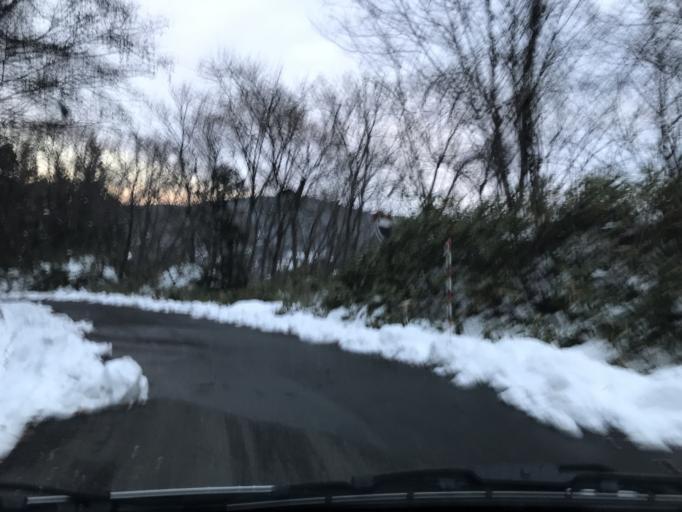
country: JP
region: Iwate
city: Mizusawa
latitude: 39.0545
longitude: 141.0332
